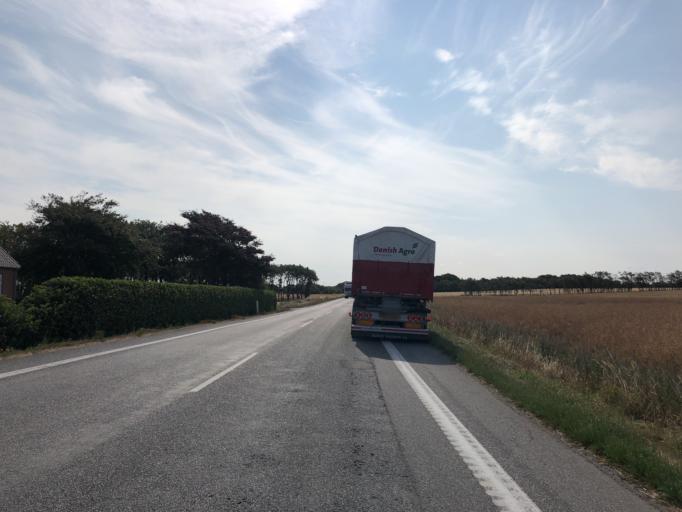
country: DK
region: Central Jutland
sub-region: Holstebro Kommune
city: Vinderup
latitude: 56.5884
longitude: 8.7984
